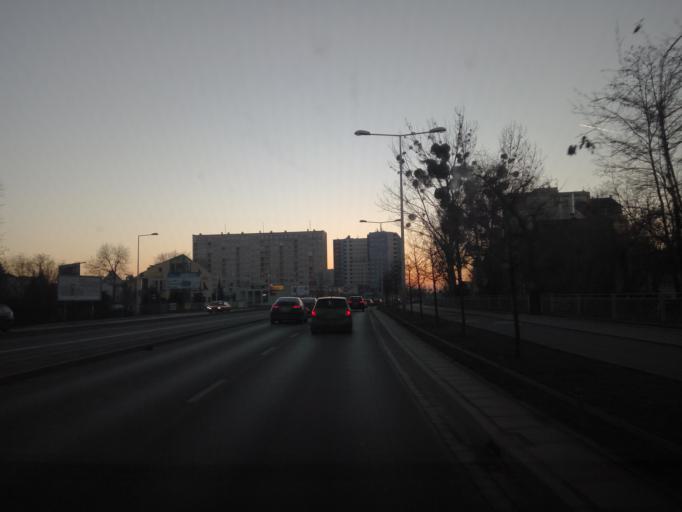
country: PL
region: Lower Silesian Voivodeship
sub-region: Powiat wroclawski
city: Wroclaw
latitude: 51.1137
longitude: 16.9642
